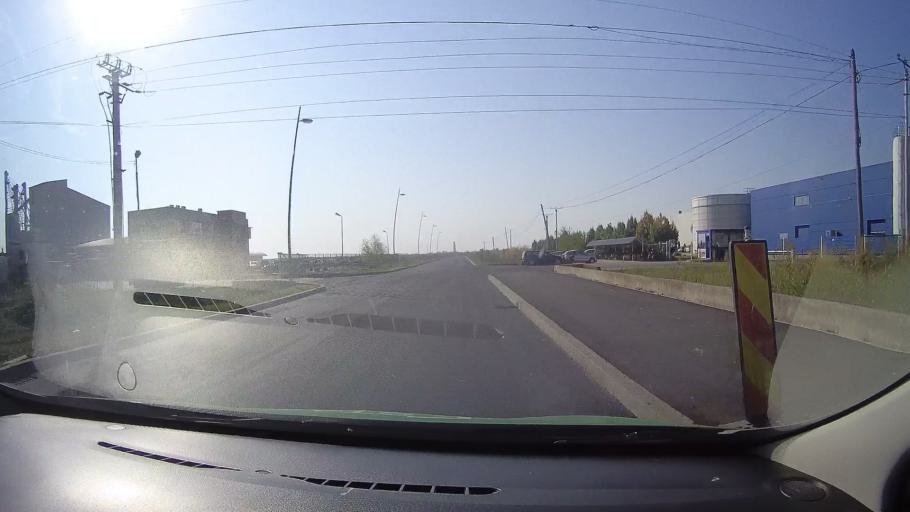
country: RO
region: Bihor
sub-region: Municipiul Salonta
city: Salonta
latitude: 46.7896
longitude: 21.6635
